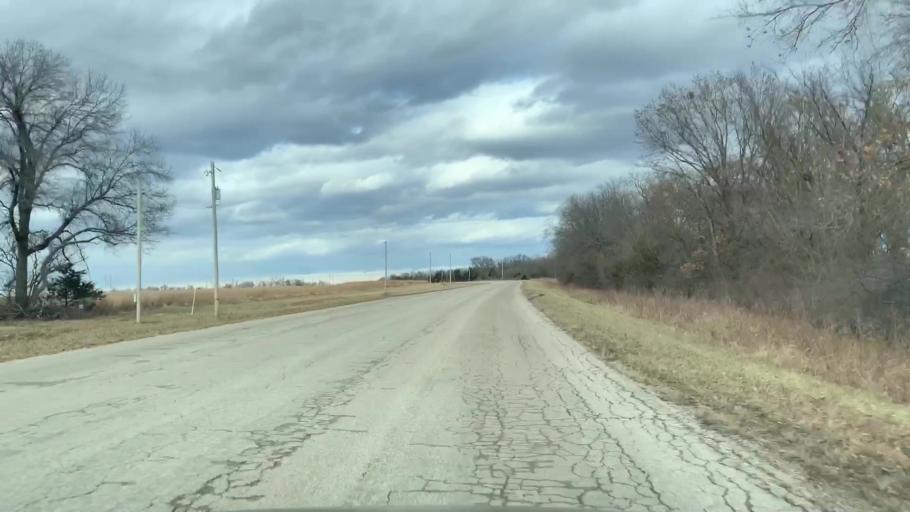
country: US
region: Kansas
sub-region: Allen County
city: Humboldt
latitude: 37.7585
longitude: -95.4716
